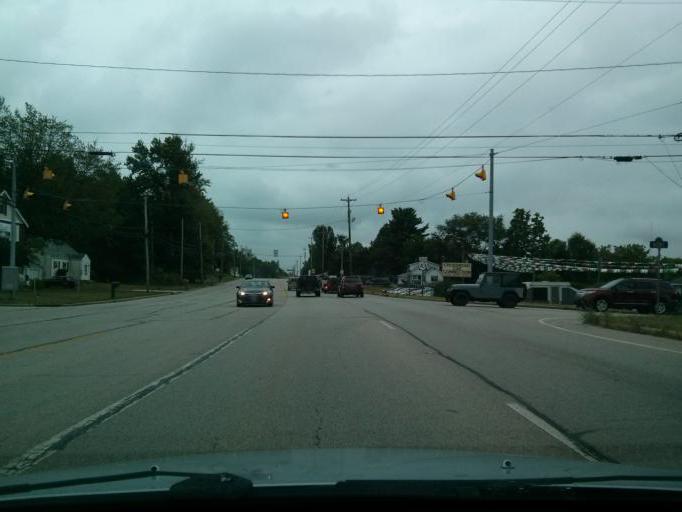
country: US
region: Ohio
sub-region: Portage County
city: Brimfield
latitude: 41.1178
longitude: -81.3486
